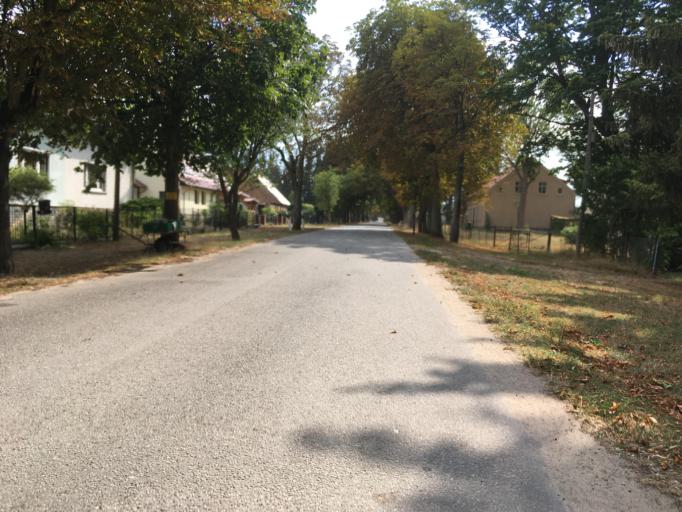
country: DE
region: Brandenburg
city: Lychen
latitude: 53.1040
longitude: 13.2892
